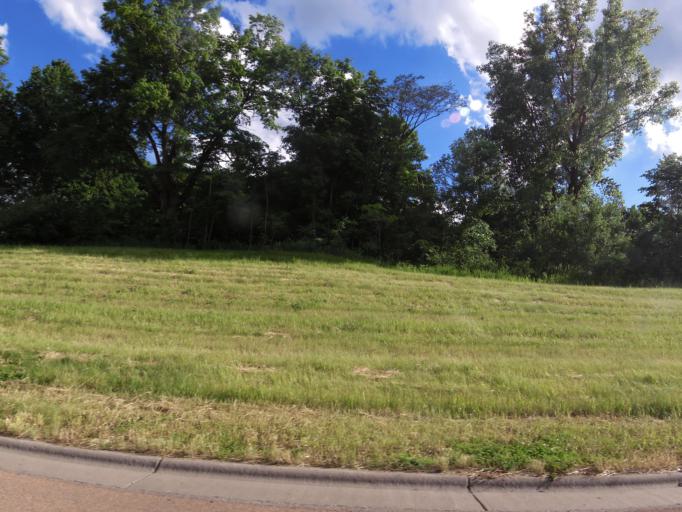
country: US
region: Minnesota
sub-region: Carver County
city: Waconia
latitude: 44.8363
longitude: -93.7715
